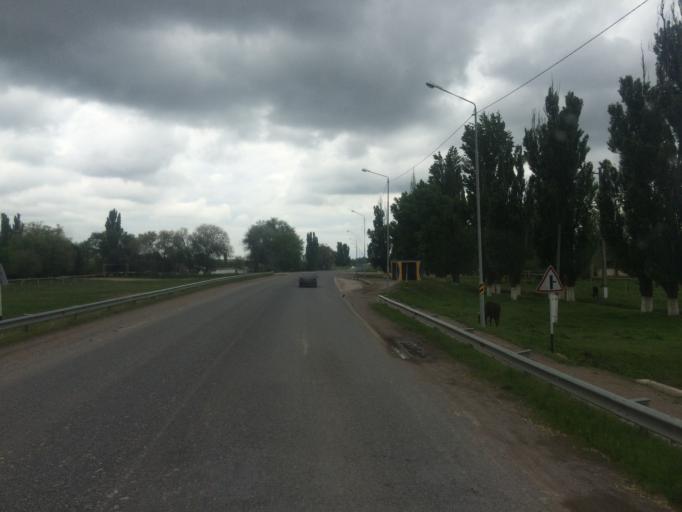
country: KZ
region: Zhambyl
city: Georgiyevka
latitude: 43.1411
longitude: 74.6187
